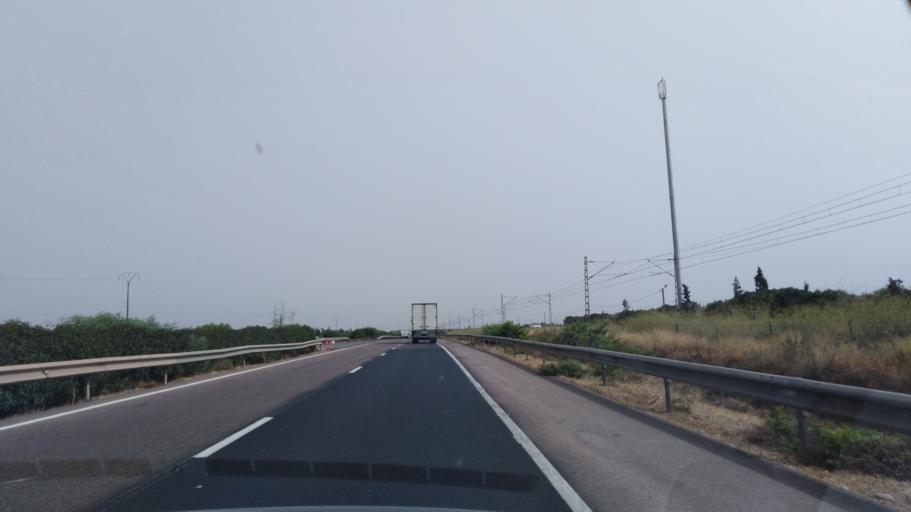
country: MA
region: Chaouia-Ouardigha
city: Nouaseur
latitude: 33.3441
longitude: -7.6135
